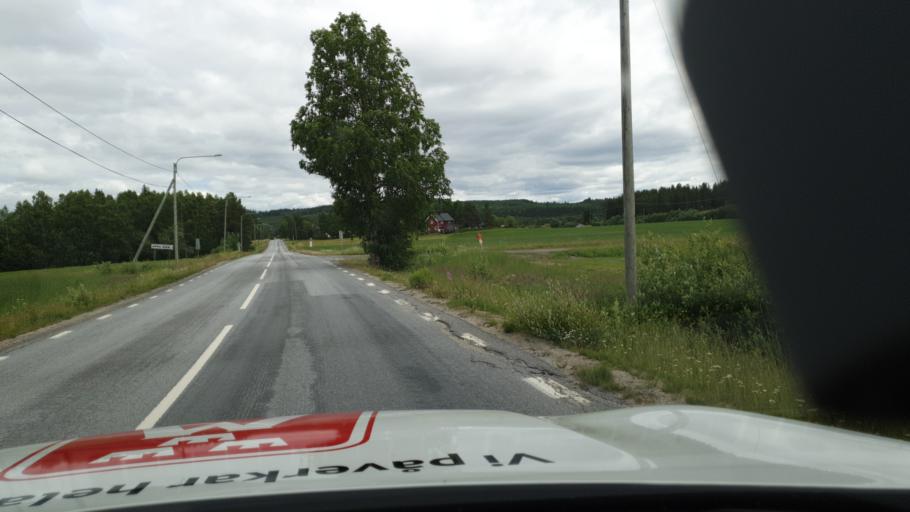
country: SE
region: Vaesterbotten
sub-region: Vannas Kommun
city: Vaennaes
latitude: 63.8969
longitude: 19.6998
